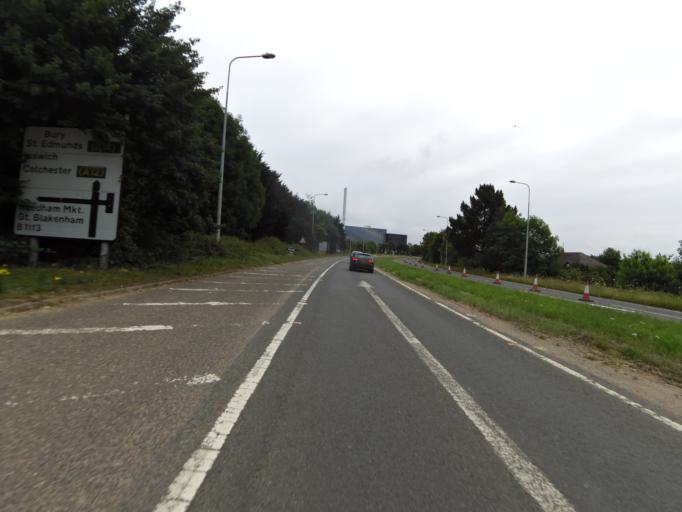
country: GB
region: England
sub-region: Suffolk
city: Bramford
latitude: 52.1007
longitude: 1.0958
